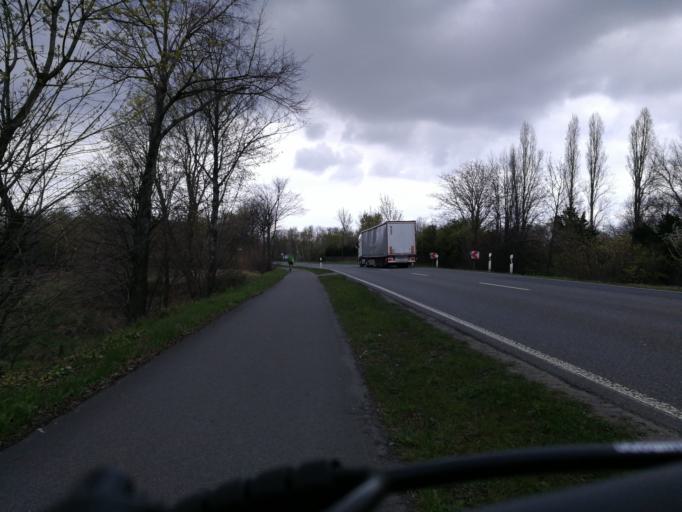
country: DE
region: North Rhine-Westphalia
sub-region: Regierungsbezirk Dusseldorf
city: Dormagen
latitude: 51.1506
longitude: 6.7888
